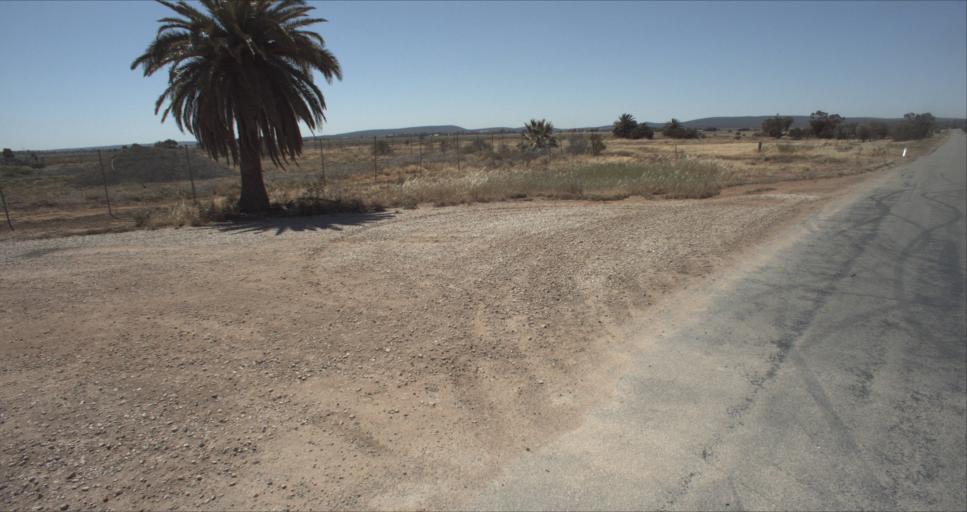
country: AU
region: New South Wales
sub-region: Leeton
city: Leeton
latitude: -34.5438
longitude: 146.4291
